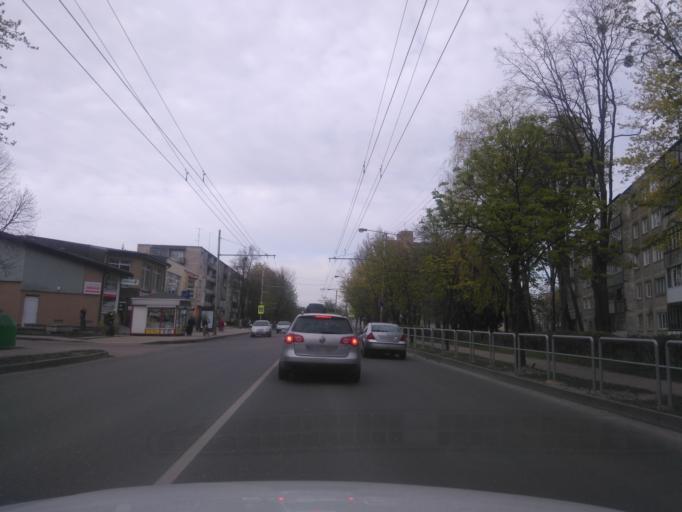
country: LT
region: Kauno apskritis
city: Dainava (Kaunas)
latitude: 54.9091
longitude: 23.9738
